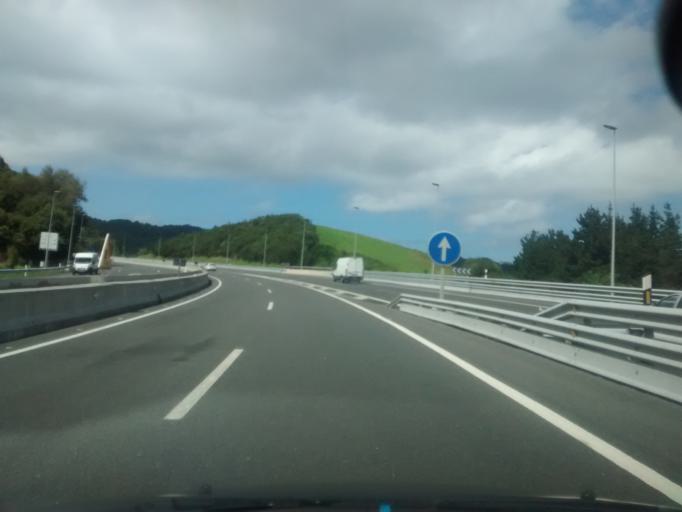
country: ES
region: Basque Country
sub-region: Provincia de Guipuzcoa
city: Usurbil
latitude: 43.2915
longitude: -2.0379
